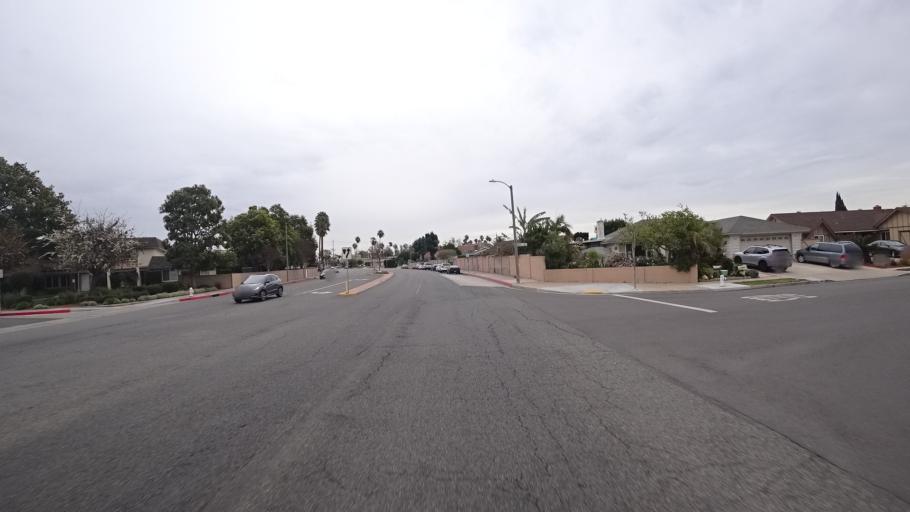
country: US
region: California
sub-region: Orange County
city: Fountain Valley
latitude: 33.7280
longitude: -117.9230
